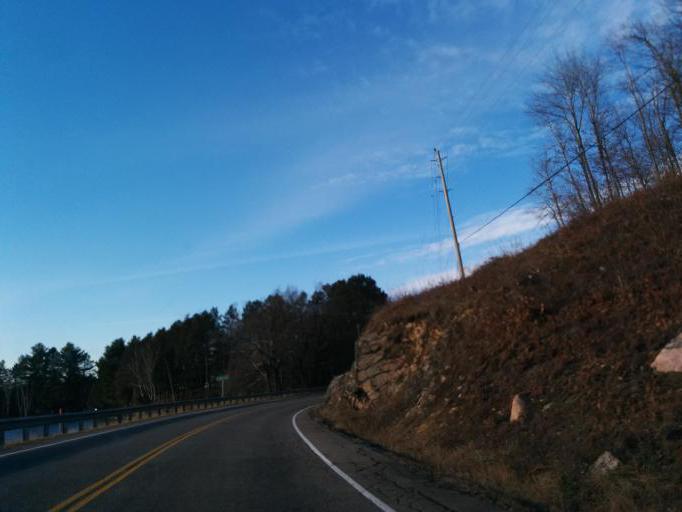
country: CA
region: Ontario
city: Bancroft
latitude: 45.0236
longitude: -78.3811
